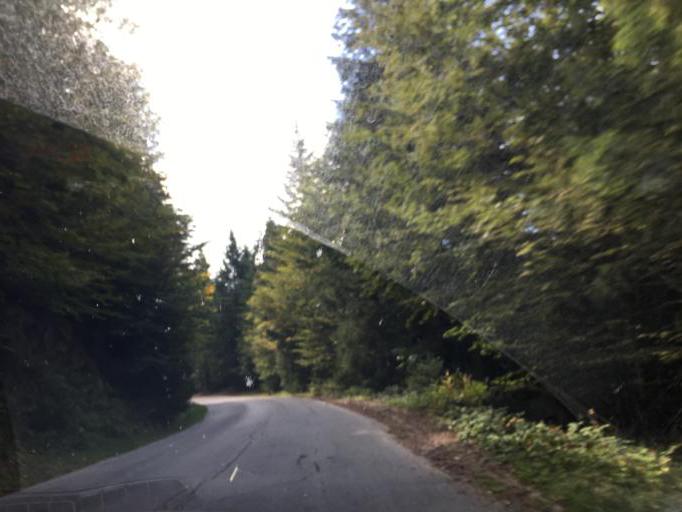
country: BG
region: Pazardzhik
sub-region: Obshtina Batak
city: Batak
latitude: 41.9152
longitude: 24.2833
